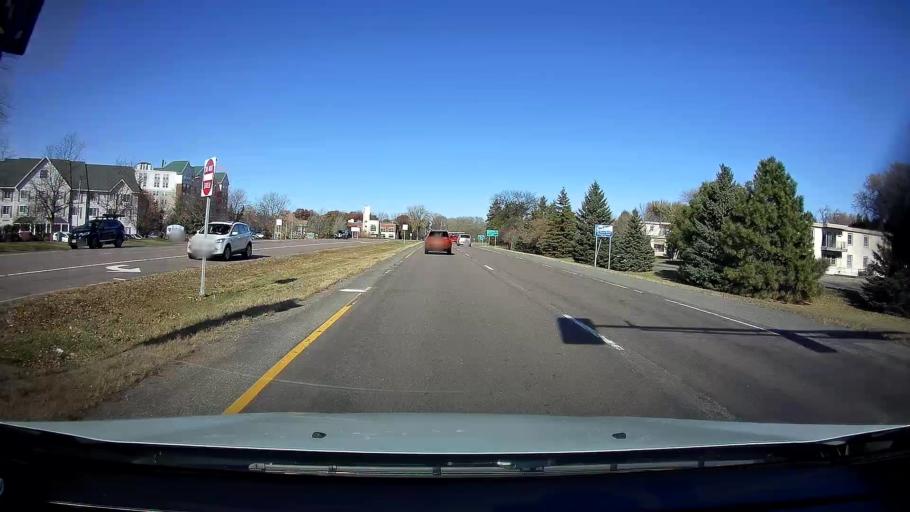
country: US
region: Minnesota
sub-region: Ramsey County
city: Roseville
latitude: 45.0281
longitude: -93.1670
